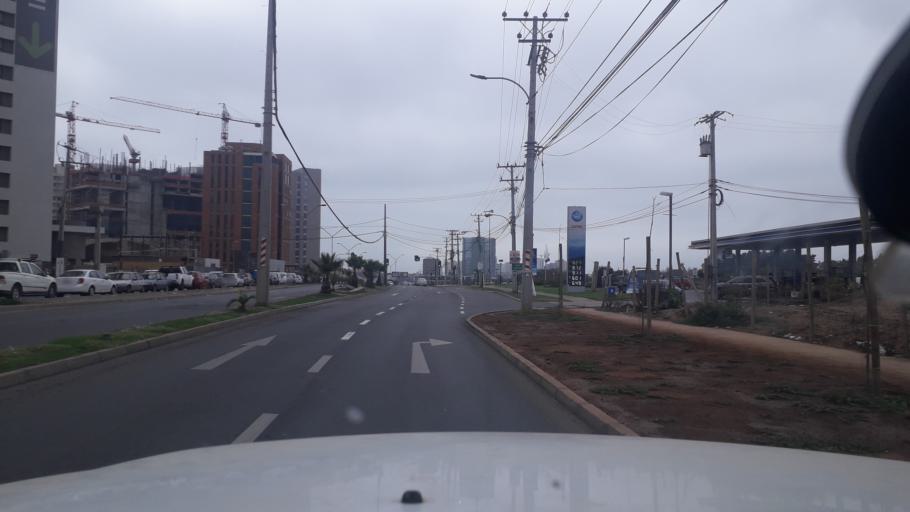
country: CL
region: Valparaiso
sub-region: Provincia de Valparaiso
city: Vina del Mar
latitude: -32.9504
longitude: -71.5447
